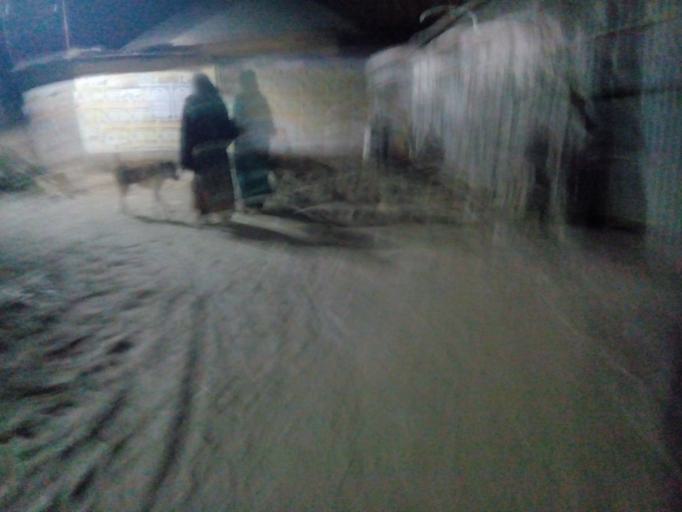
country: BD
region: Dhaka
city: Paltan
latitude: 23.7466
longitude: 90.4202
